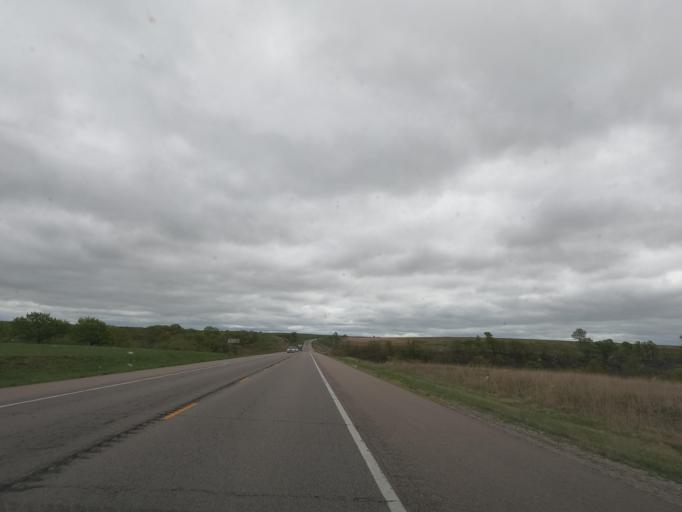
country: US
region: Kansas
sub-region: Greenwood County
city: Eureka
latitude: 37.6560
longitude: -96.4732
